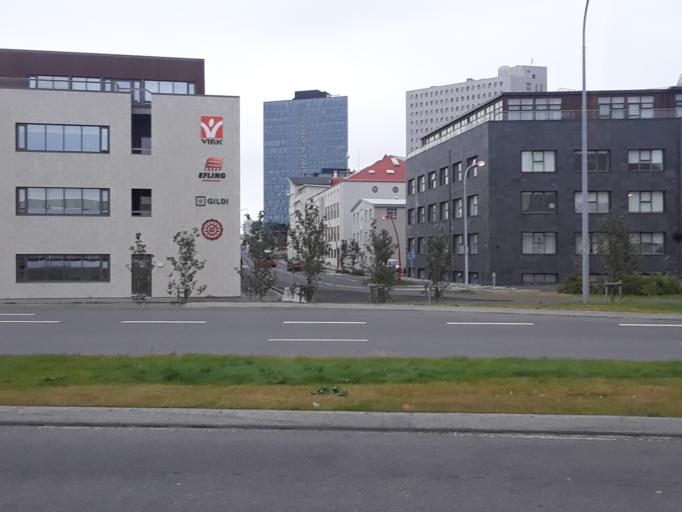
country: IS
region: Capital Region
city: Reykjavik
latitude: 64.1450
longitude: -21.9150
